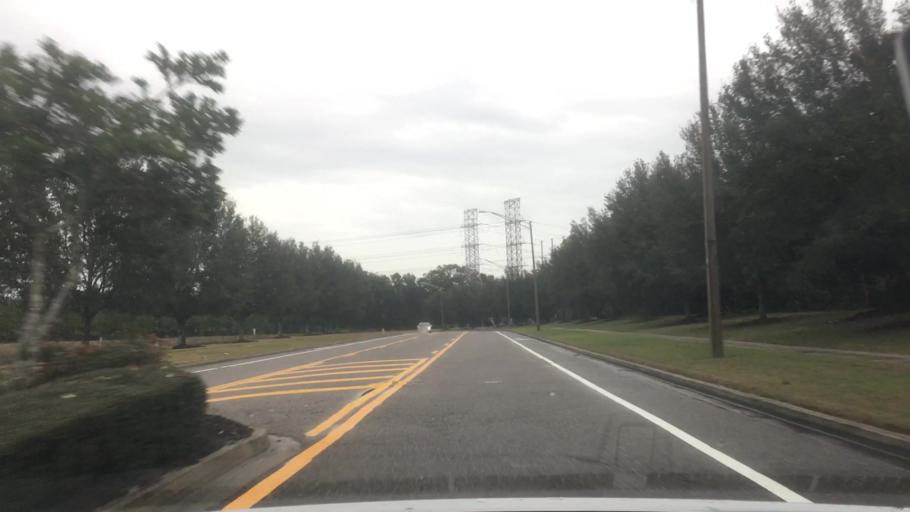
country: US
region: Florida
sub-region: Duval County
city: Jacksonville
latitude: 30.4486
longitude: -81.5773
